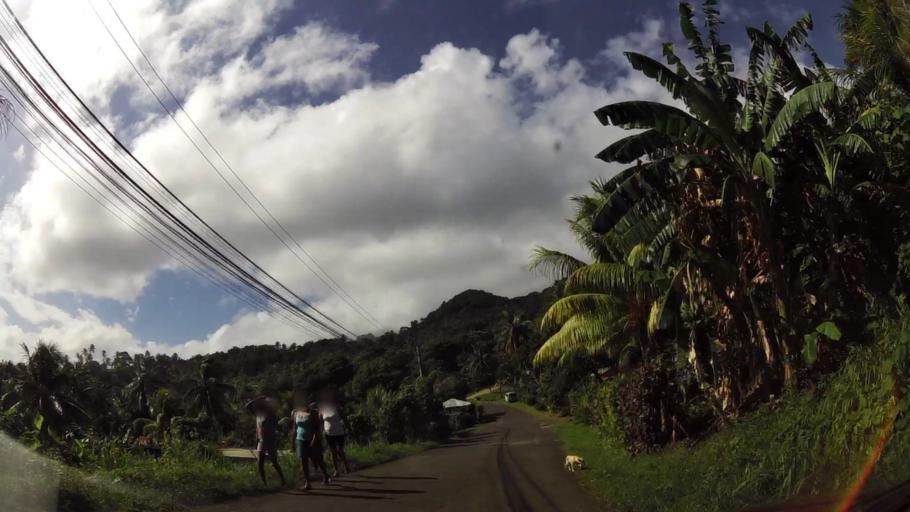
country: DM
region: Saint David
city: Castle Bruce
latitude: 15.4829
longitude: -61.2521
